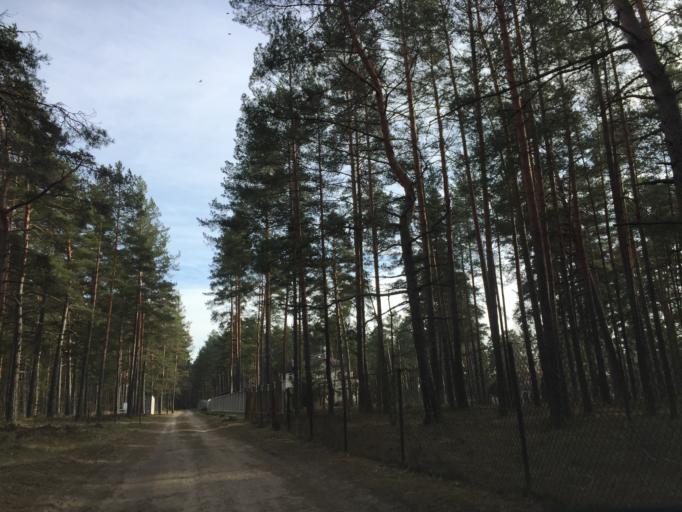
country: LV
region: Adazi
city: Adazi
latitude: 57.1228
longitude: 24.3372
